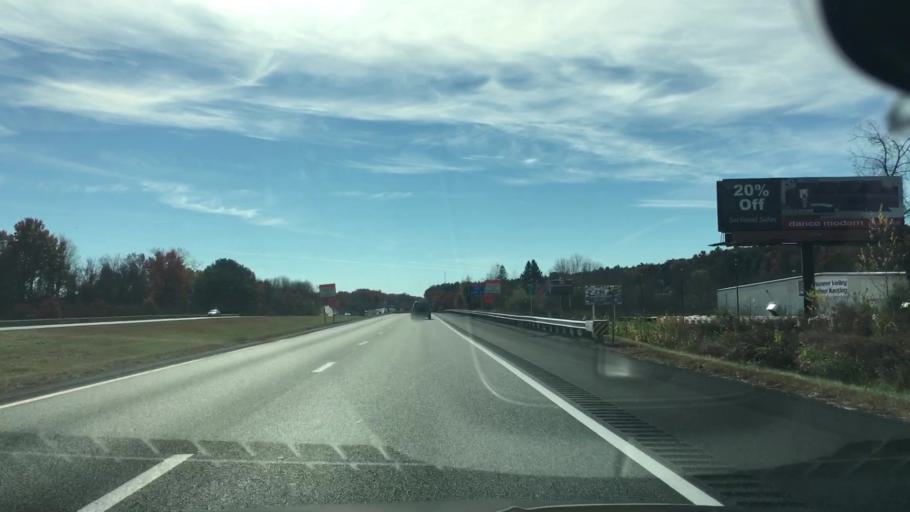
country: US
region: Massachusetts
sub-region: Hampshire County
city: Hatfield
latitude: 42.3683
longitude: -72.6346
